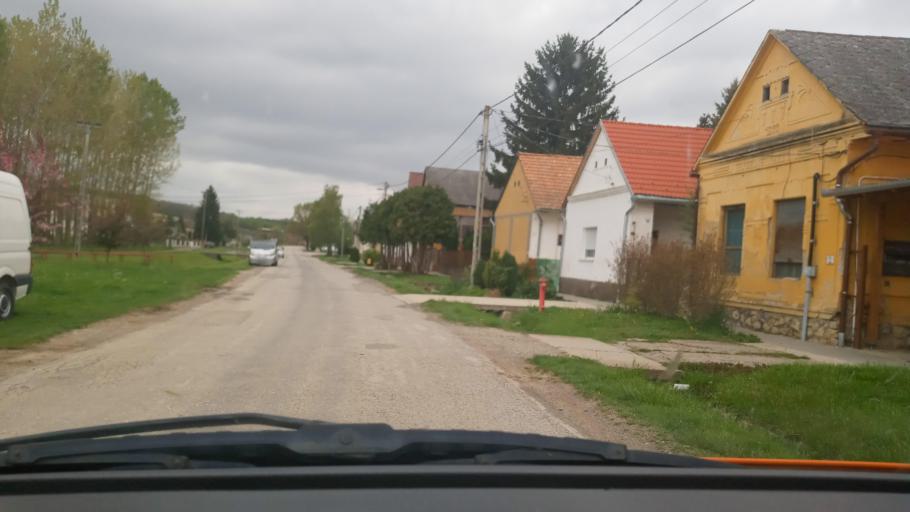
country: HU
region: Baranya
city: Boly
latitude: 46.0040
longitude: 18.5524
